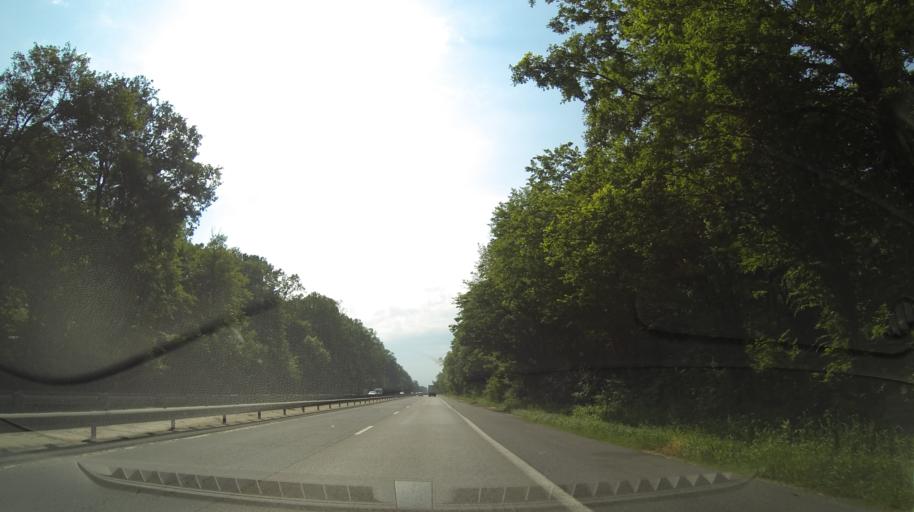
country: RO
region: Giurgiu
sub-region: Comuna Vanatorii Mici
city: Vanatorii Mici
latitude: 44.5100
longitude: 25.5680
